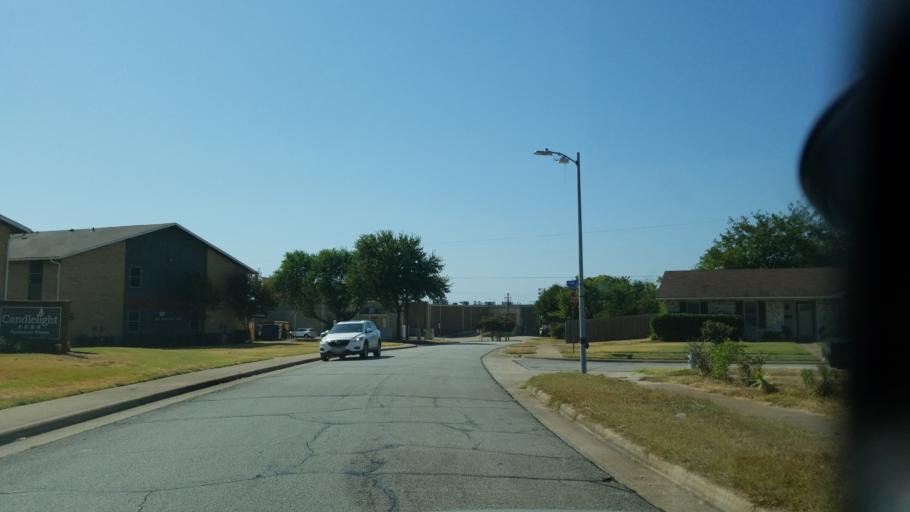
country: US
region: Texas
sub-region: Dallas County
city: Duncanville
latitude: 32.6349
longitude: -96.9027
